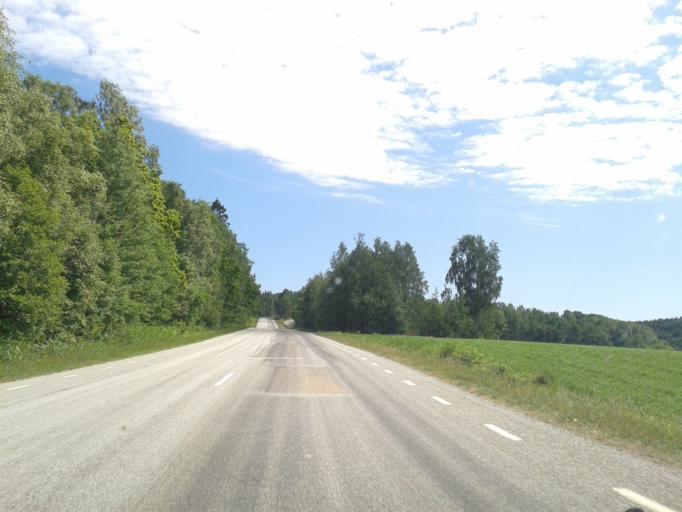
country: SE
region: Vaestra Goetaland
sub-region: Uddevalla Kommun
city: Ljungskile
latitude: 58.1848
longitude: 11.9534
